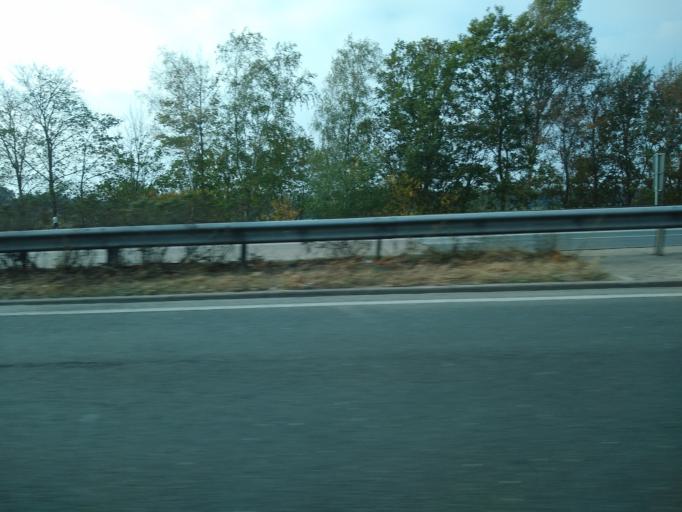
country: DE
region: Lower Saxony
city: Oldenburg
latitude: 53.1230
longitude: 8.2753
